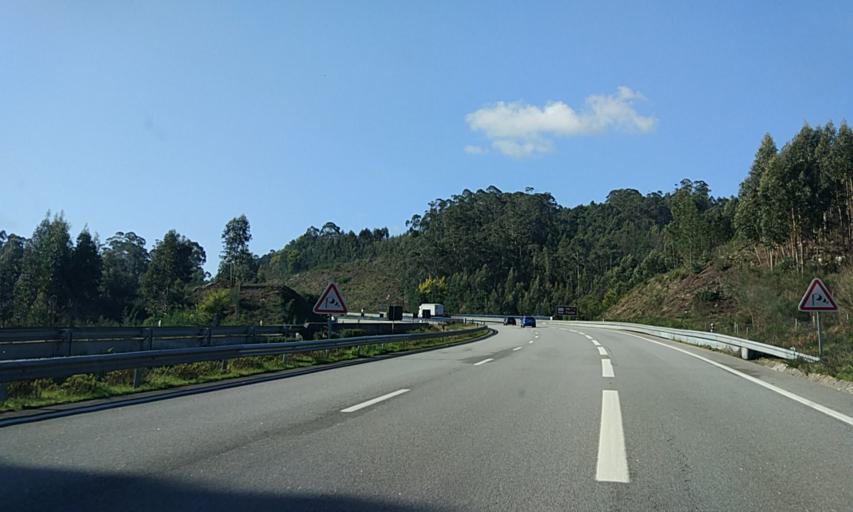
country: PT
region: Aveiro
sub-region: Sever do Vouga
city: Sever do Vouga
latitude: 40.6799
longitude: -8.2769
